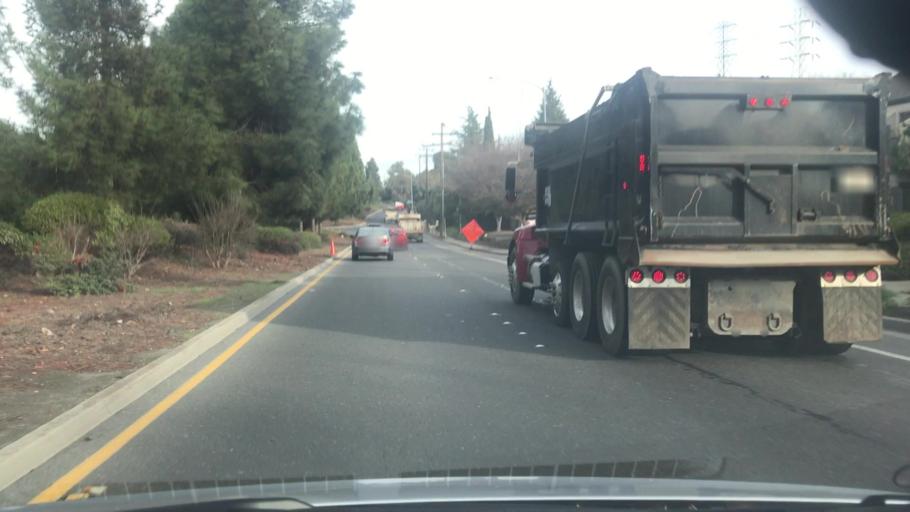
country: US
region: California
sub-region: Santa Clara County
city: Cupertino
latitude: 37.3270
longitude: -122.0689
